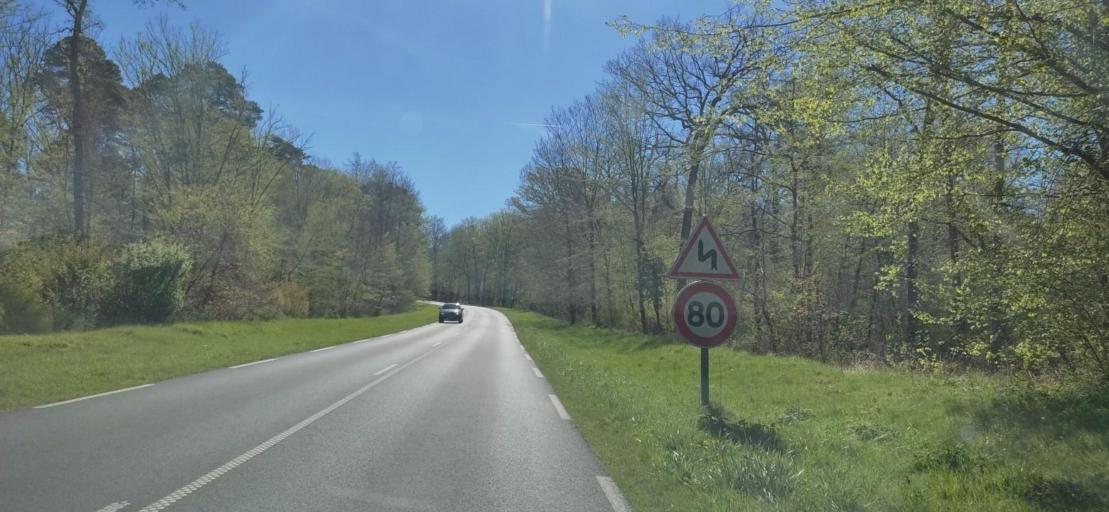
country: FR
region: Picardie
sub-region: Departement de l'Oise
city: Choisy-au-Bac
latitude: 49.3832
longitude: 2.9013
